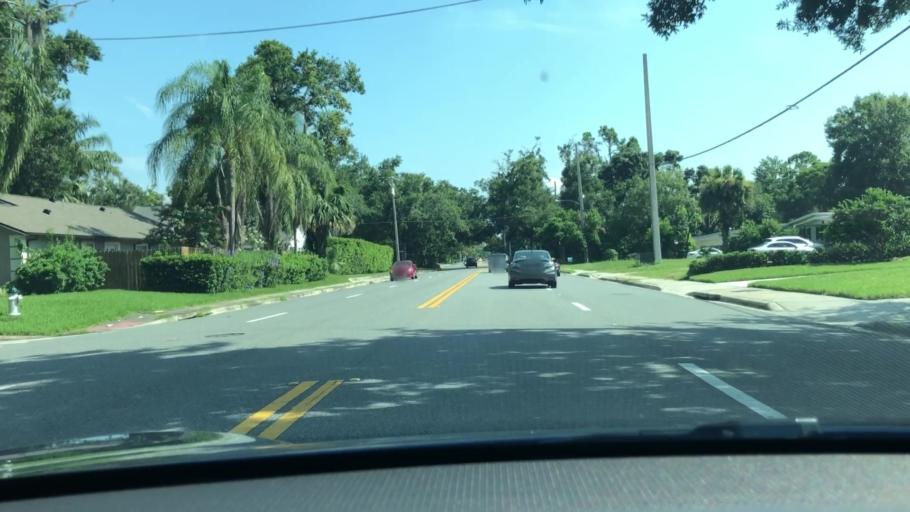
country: US
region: Florida
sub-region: Orange County
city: Winter Park
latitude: 28.6025
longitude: -81.3280
